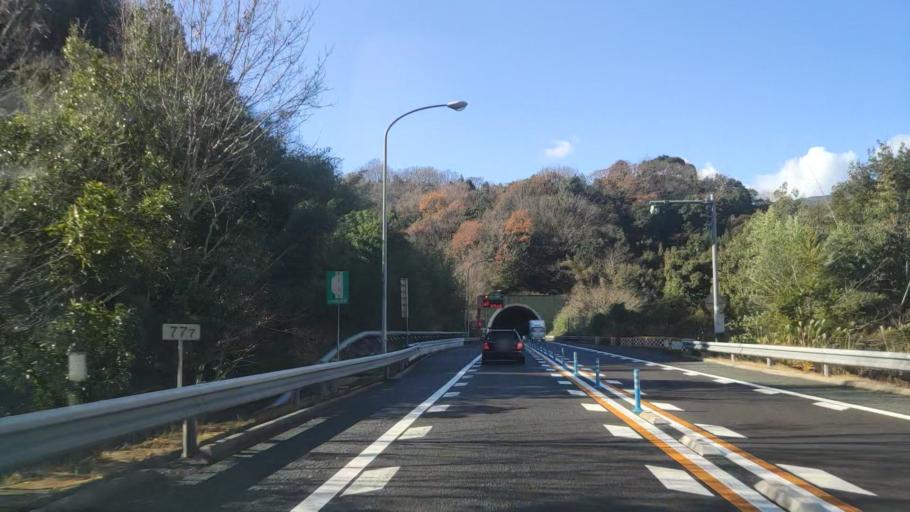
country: JP
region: Tokushima
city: Ikedacho
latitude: 34.0219
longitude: 133.8003
